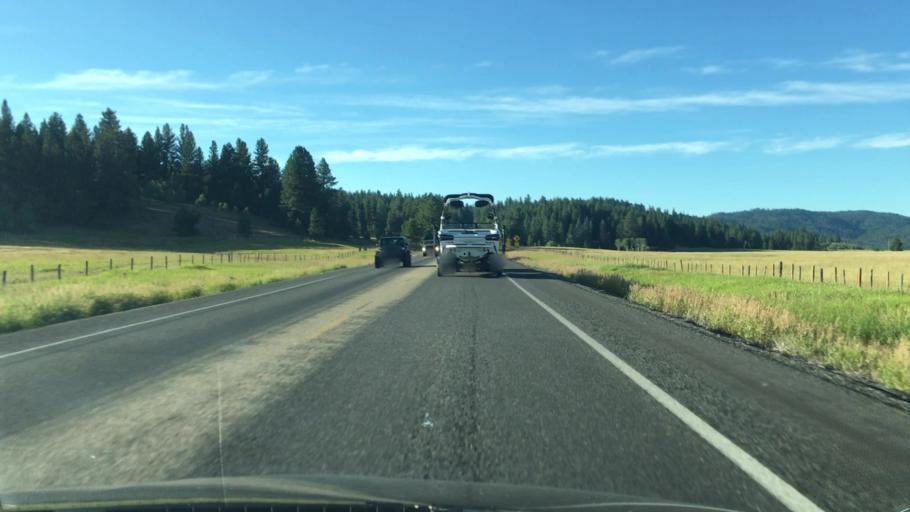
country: US
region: Idaho
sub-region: Valley County
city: Cascade
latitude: 44.5534
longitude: -116.0279
